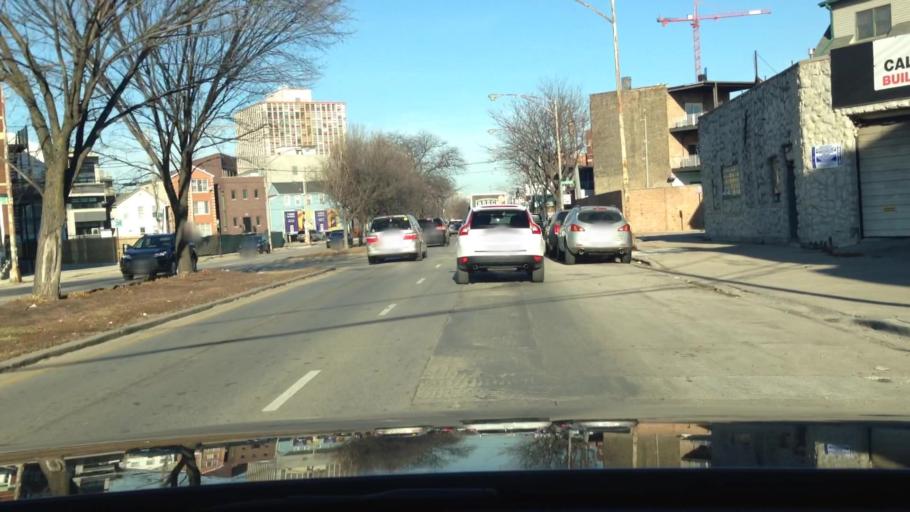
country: US
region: Illinois
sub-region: Cook County
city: Chicago
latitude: 41.8915
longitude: -87.6586
